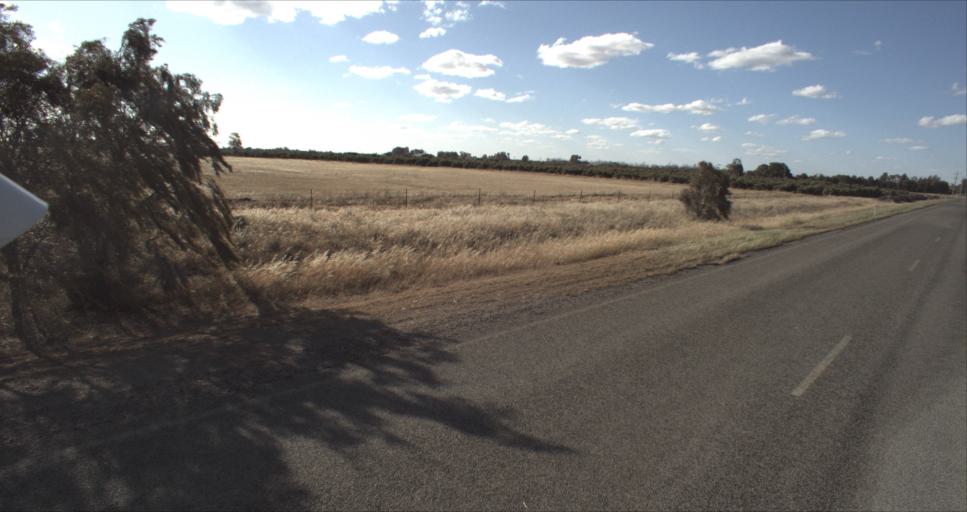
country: AU
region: New South Wales
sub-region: Leeton
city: Leeton
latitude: -34.5310
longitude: 146.2814
